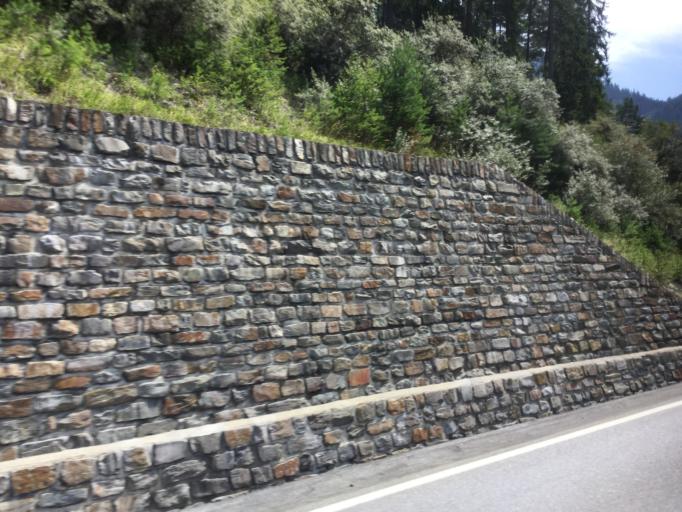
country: CH
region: Grisons
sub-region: Albula District
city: Tiefencastel
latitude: 46.6482
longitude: 9.5809
